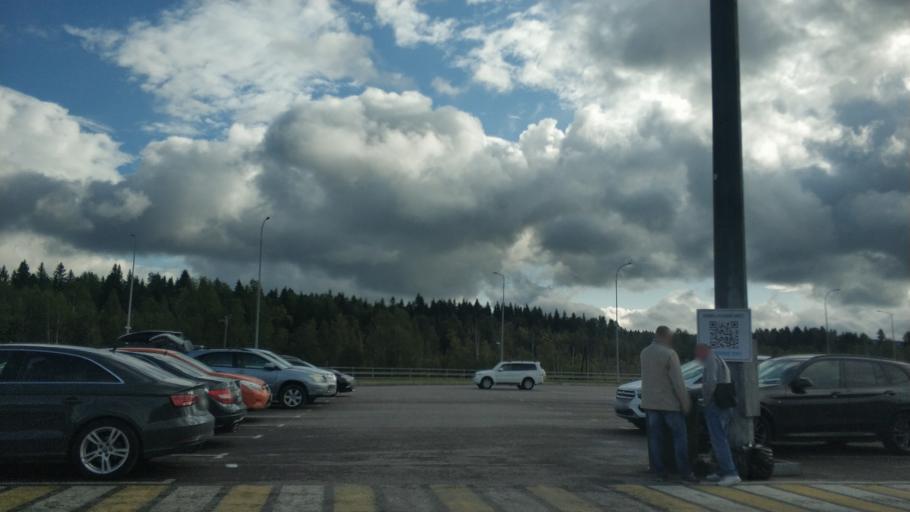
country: RU
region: Republic of Karelia
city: Ruskeala
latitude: 61.9489
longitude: 30.5841
